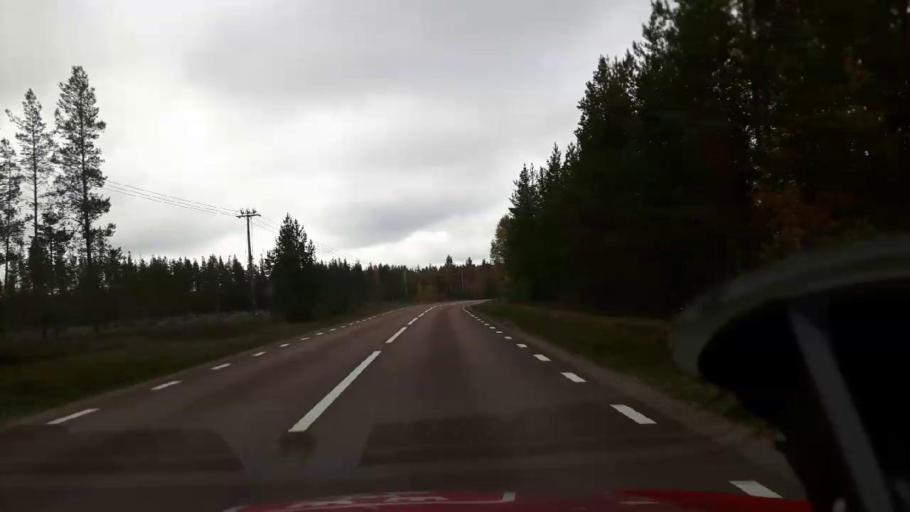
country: SE
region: Jaemtland
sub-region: Harjedalens Kommun
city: Sveg
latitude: 62.2250
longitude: 14.8475
